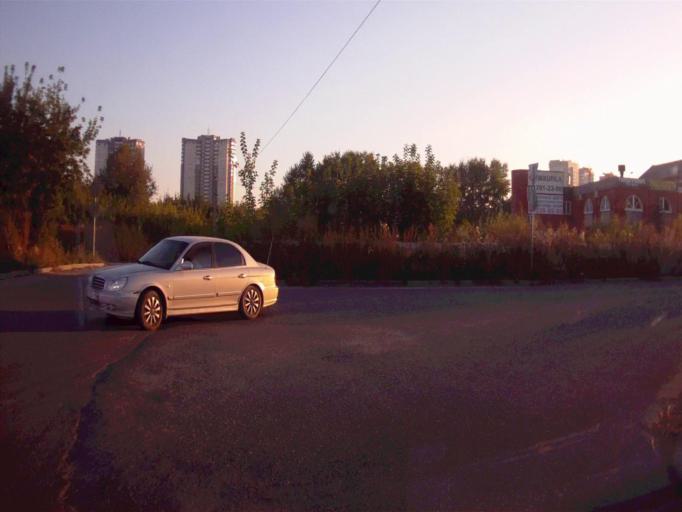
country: RU
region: Chelyabinsk
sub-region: Gorod Chelyabinsk
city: Chelyabinsk
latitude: 55.1751
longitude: 61.3800
